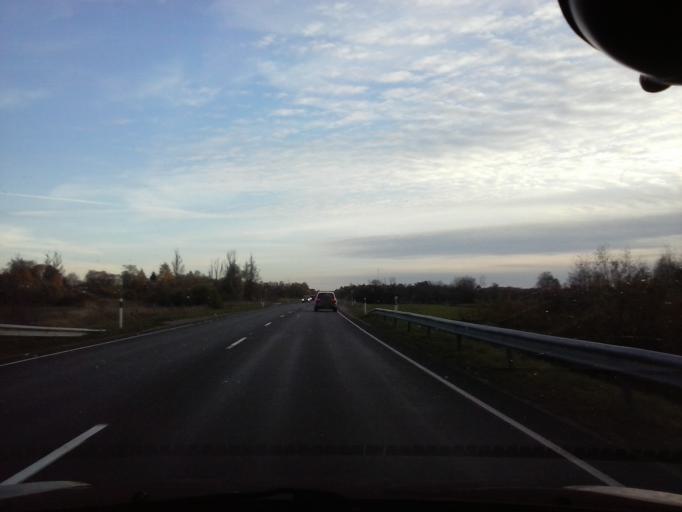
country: EE
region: Harju
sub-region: Nissi vald
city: Turba
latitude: 58.9194
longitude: 24.1129
